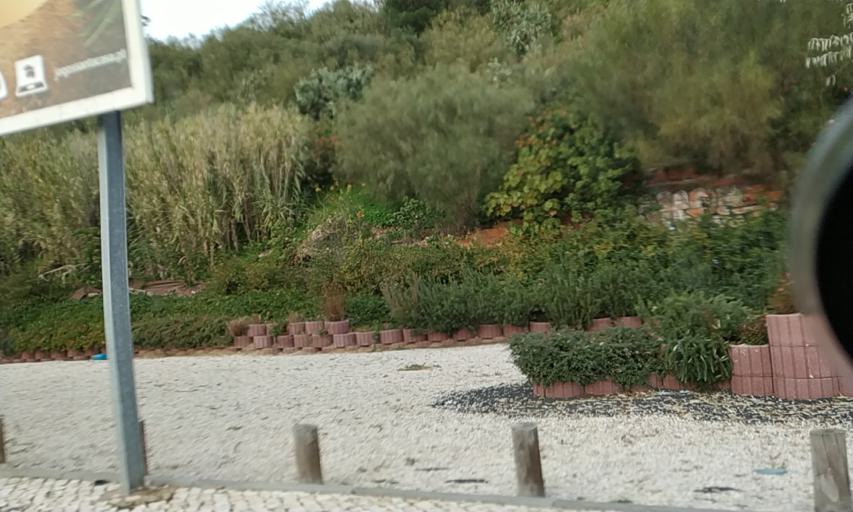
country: PT
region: Setubal
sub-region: Setubal
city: Setubal
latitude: 38.5205
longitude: -8.8795
